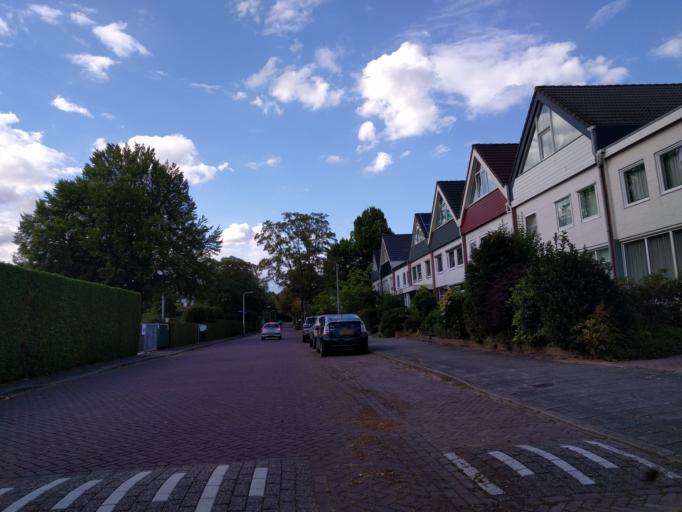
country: NL
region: Gelderland
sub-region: Gemeente Nijmegen
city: Nijmegen
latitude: 51.8227
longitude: 5.8759
